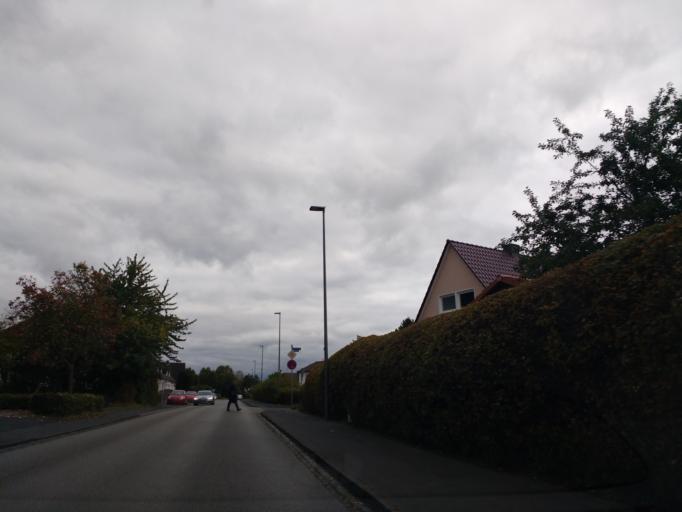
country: DE
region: Hesse
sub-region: Regierungsbezirk Kassel
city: Lohfelden
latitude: 51.2907
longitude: 9.5386
